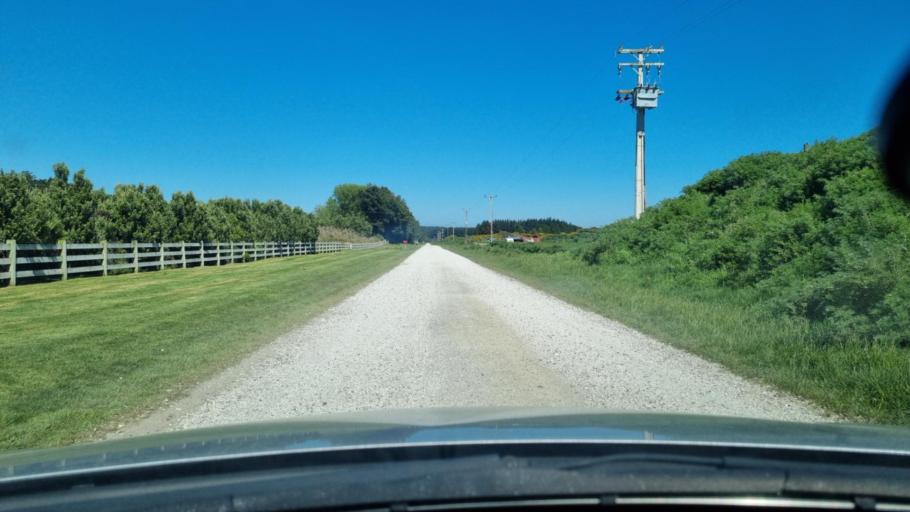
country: NZ
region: Southland
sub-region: Invercargill City
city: Invercargill
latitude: -46.4537
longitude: 168.2771
